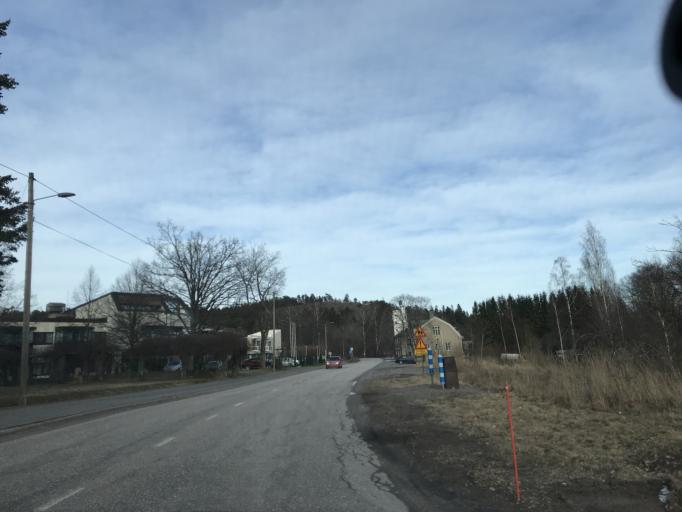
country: FI
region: Uusimaa
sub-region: Raaseporin
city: Pohja
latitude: 60.0955
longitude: 23.5240
